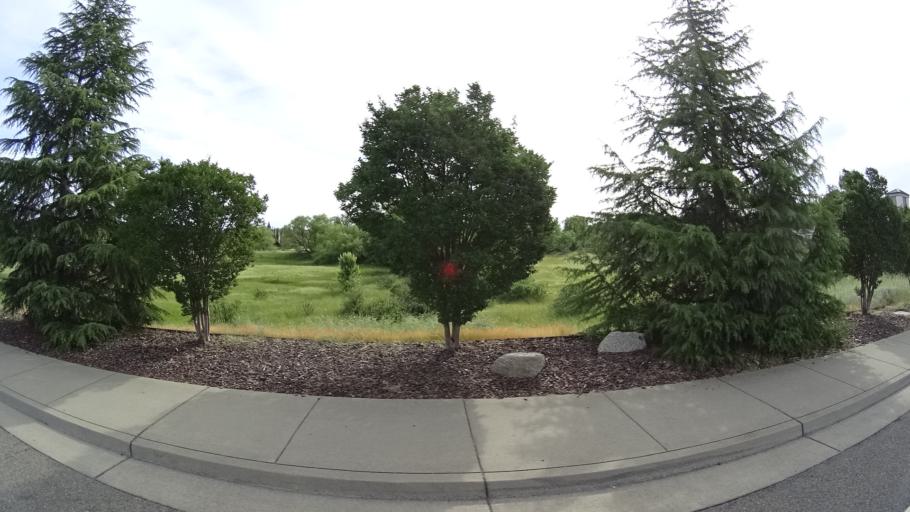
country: US
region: California
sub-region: Placer County
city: Rocklin
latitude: 38.8202
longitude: -121.2816
